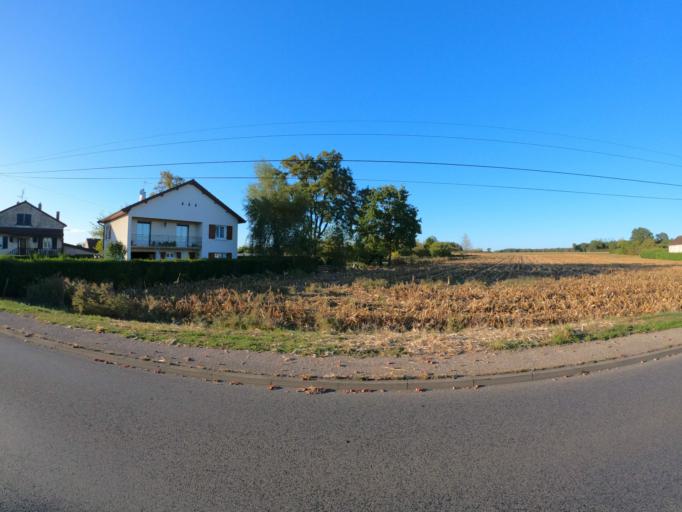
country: FR
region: Bourgogne
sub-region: Departement de Saone-et-Loire
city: Saint-Marcel
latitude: 46.7838
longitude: 4.9289
